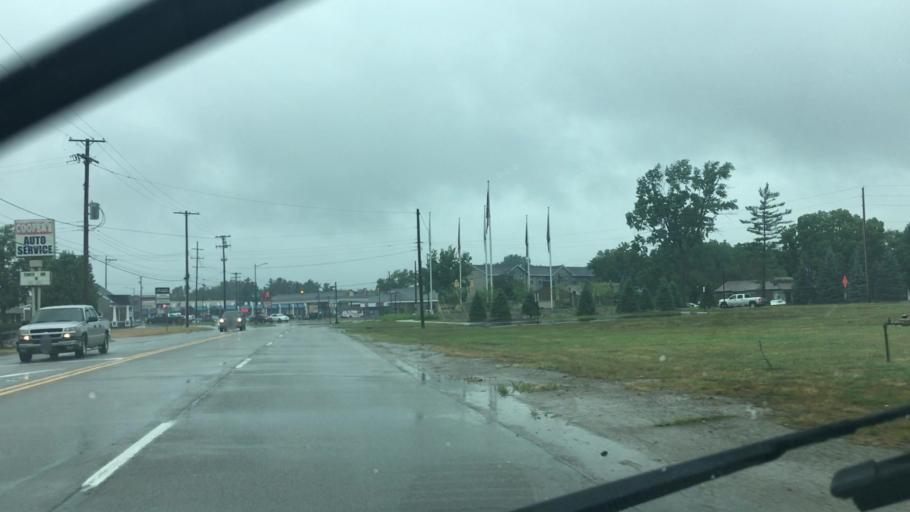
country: US
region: Michigan
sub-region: Ottawa County
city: Jenison
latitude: 42.9062
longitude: -85.7870
